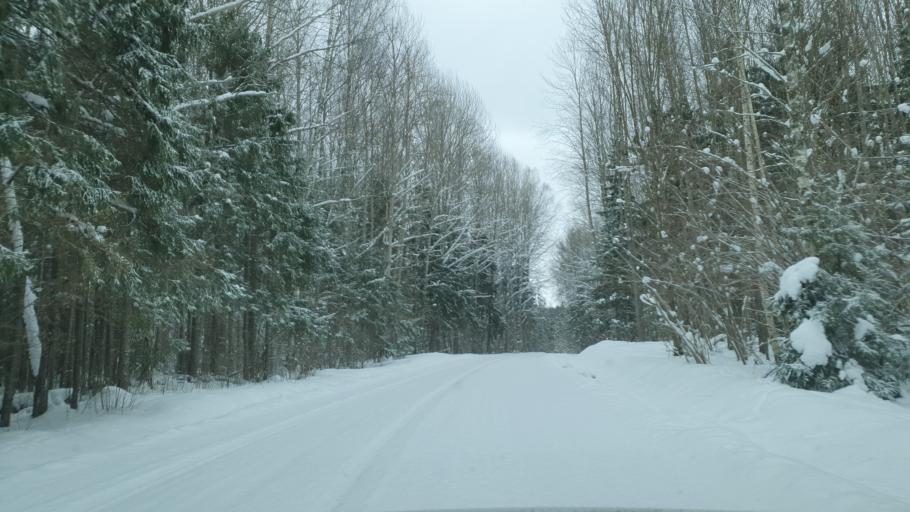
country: EE
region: Polvamaa
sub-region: Raepina vald
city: Rapina
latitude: 58.1970
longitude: 27.3305
